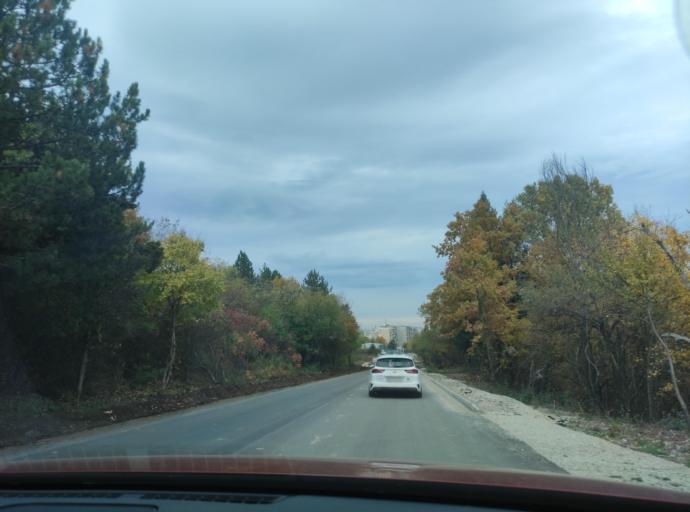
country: BG
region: Montana
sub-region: Obshtina Montana
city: Montana
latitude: 43.3928
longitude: 23.2412
